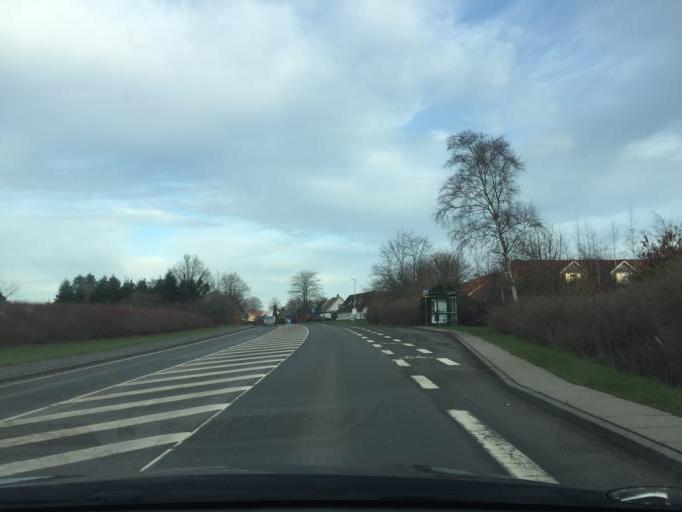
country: DK
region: South Denmark
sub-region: Faaborg-Midtfyn Kommune
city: Ringe
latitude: 55.2283
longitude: 10.4656
